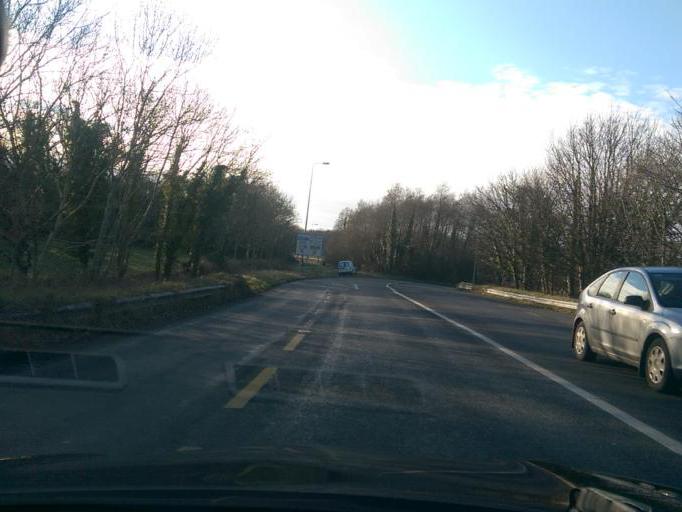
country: IE
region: Connaught
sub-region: County Galway
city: Oranmore
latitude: 53.2749
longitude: -8.9816
